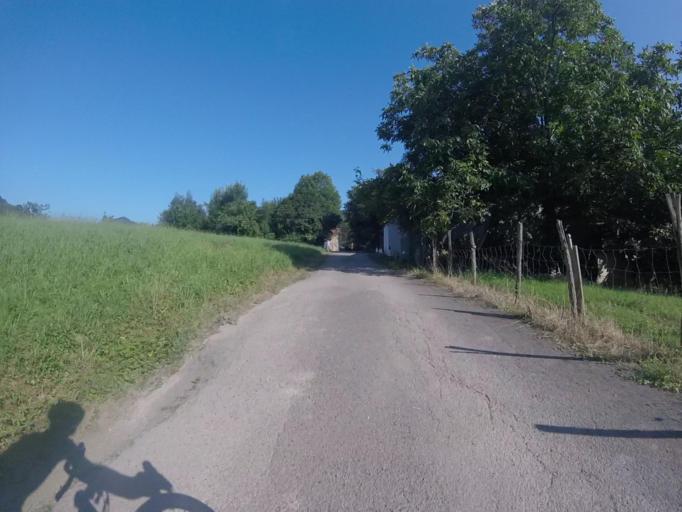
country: ES
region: Basque Country
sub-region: Provincia de Guipuzcoa
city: Astigarraga
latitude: 43.2577
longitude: -1.9417
